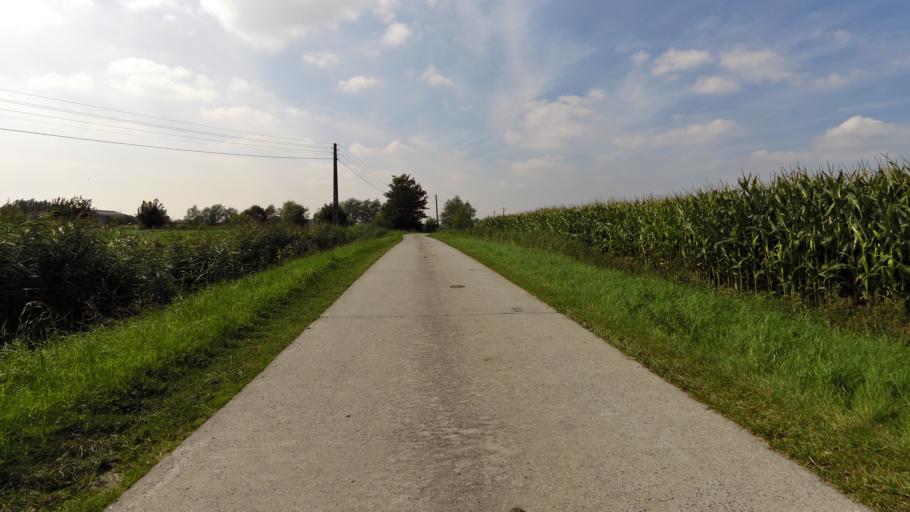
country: BE
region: Flanders
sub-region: Provincie West-Vlaanderen
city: Ostend
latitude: 51.1599
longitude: 2.8883
